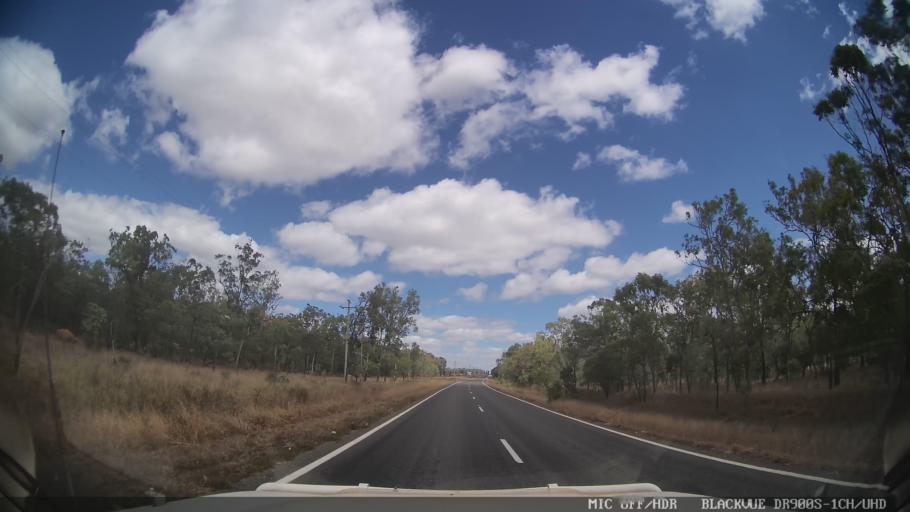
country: AU
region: Queensland
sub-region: Tablelands
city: Ravenshoe
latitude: -18.0331
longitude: 144.8697
